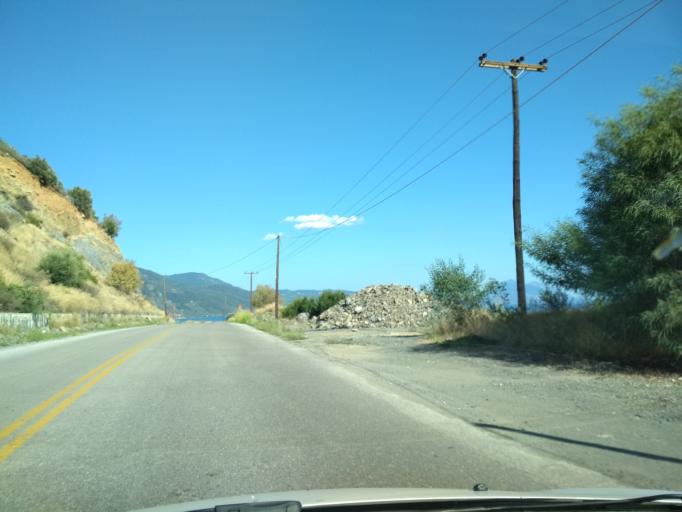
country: GR
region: Central Greece
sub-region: Nomos Evvoias
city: Oreoi
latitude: 38.8436
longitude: 23.1073
